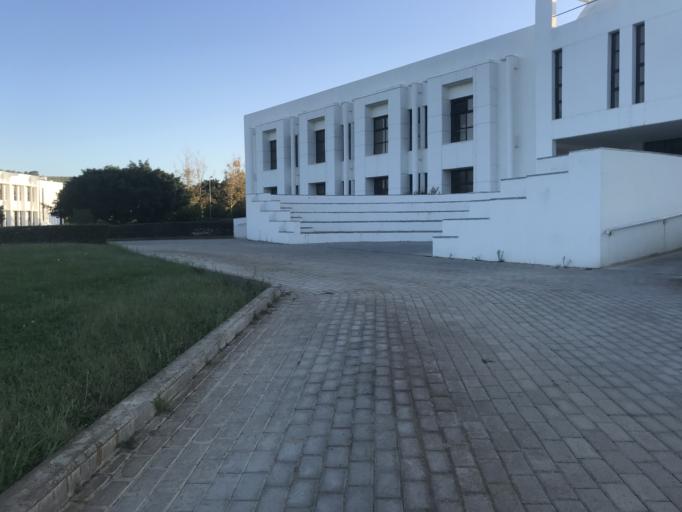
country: GR
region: Crete
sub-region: Nomos Irakleiou
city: Gazi
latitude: 35.3053
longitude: 25.0727
